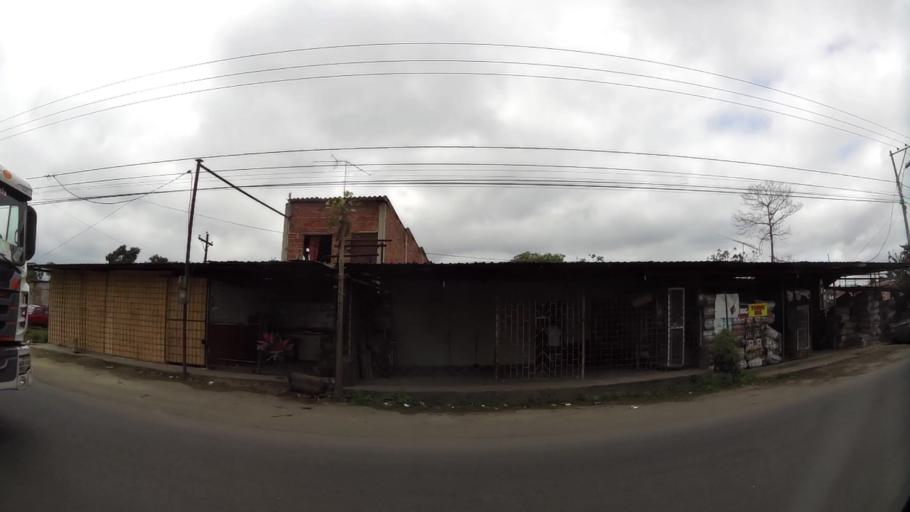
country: EC
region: Guayas
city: Naranjal
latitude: -2.6829
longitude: -79.6234
